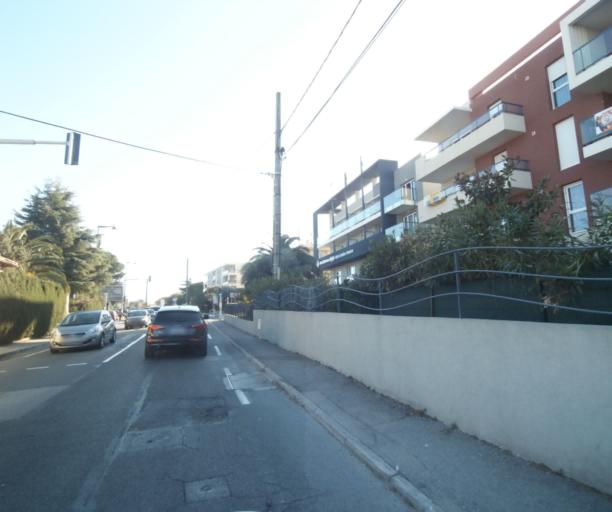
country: FR
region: Provence-Alpes-Cote d'Azur
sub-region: Departement des Alpes-Maritimes
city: Antibes
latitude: 43.5942
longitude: 7.1200
